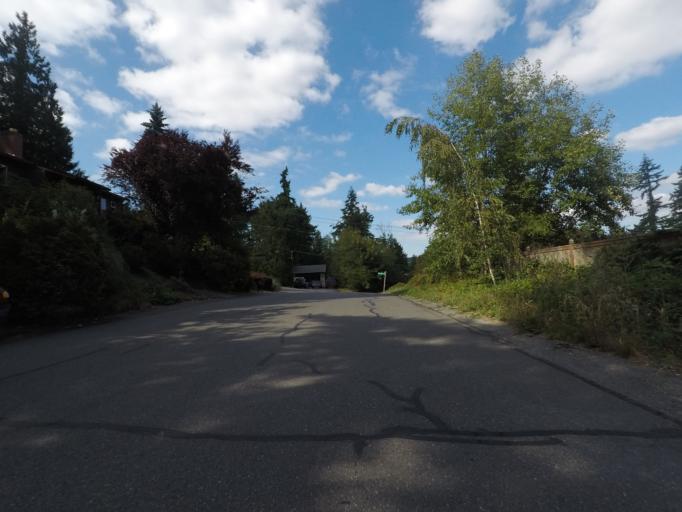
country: US
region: Washington
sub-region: King County
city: Kenmore
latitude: 47.7721
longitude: -122.2504
